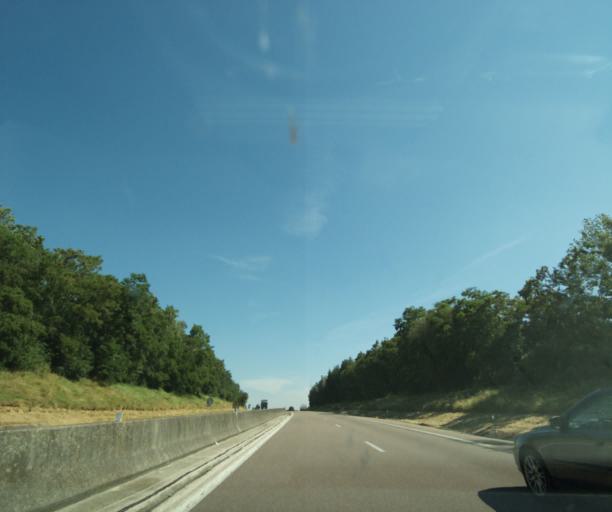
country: FR
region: Lorraine
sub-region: Departement des Vosges
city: Chatenois
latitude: 48.3782
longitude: 5.8815
